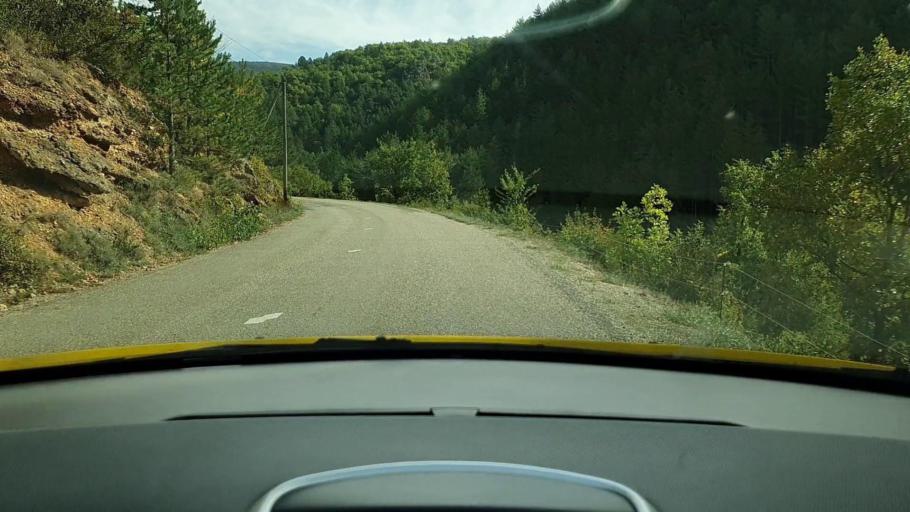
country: FR
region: Languedoc-Roussillon
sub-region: Departement de la Lozere
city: Meyrueis
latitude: 44.0769
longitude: 3.3714
